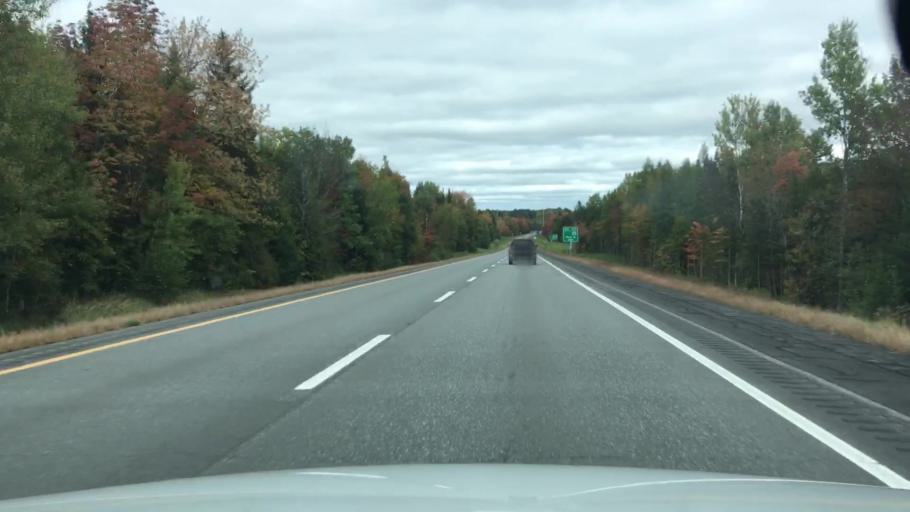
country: US
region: Maine
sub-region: Somerset County
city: Pittsfield
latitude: 44.7718
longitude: -69.4092
